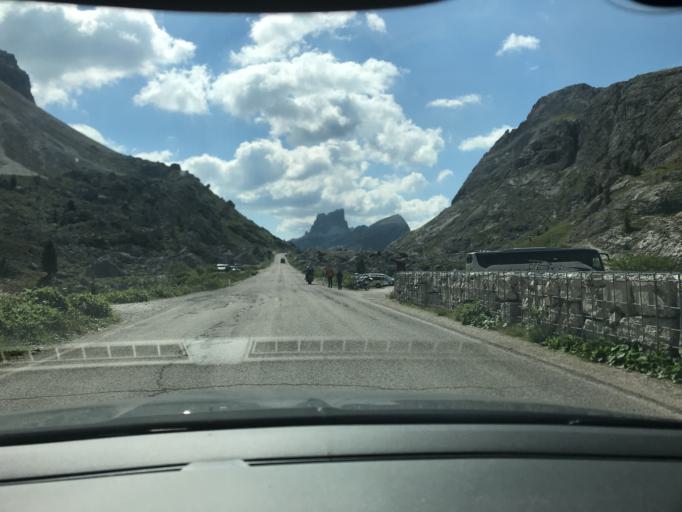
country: IT
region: Veneto
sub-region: Provincia di Belluno
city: Livinallongo del Col di Lana
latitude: 46.5282
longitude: 11.9915
